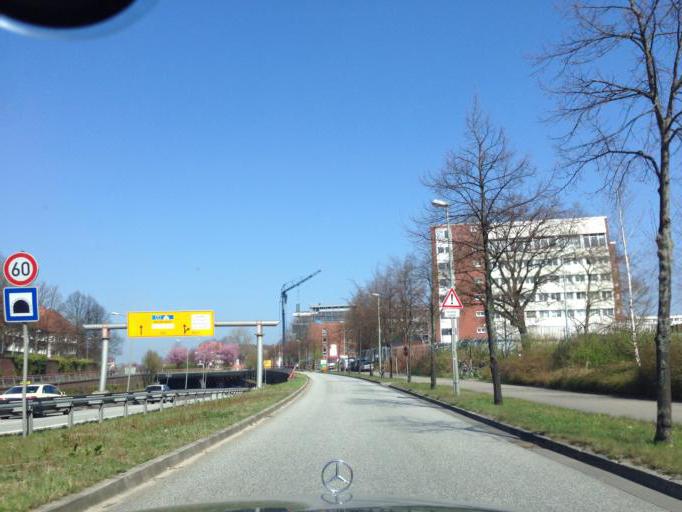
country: DE
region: Hamburg
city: Alsterdorf
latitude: 53.6211
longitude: 10.0133
